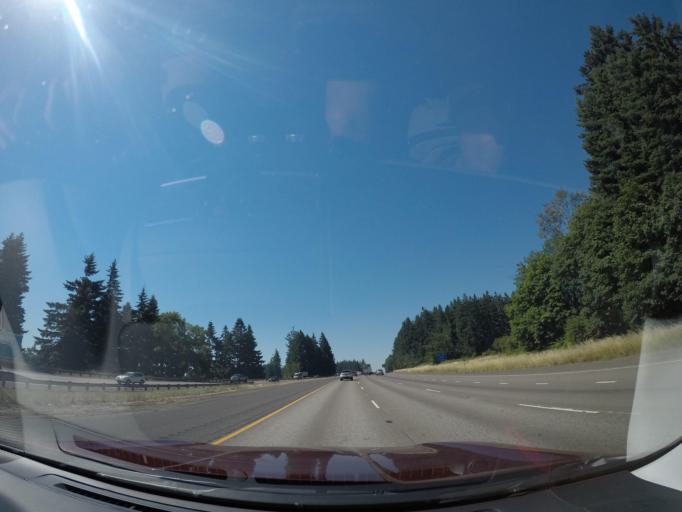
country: US
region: Oregon
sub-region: Clackamas County
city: Wilsonville
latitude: 45.2744
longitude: -122.7776
